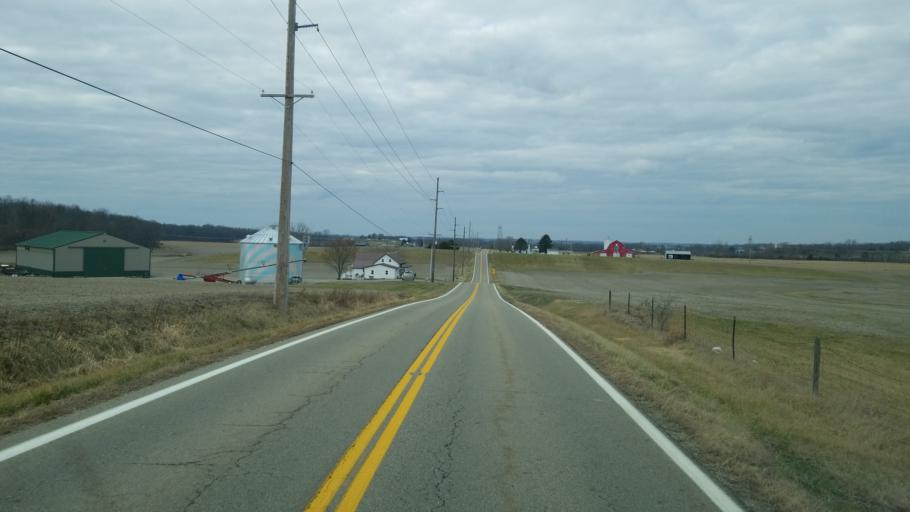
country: US
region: Ohio
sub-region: Ross County
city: Frankfort
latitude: 39.3552
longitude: -83.2610
